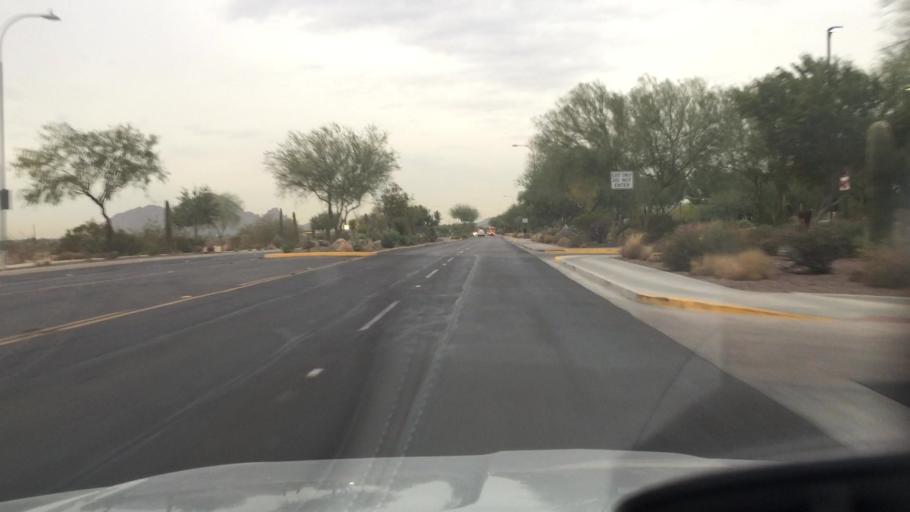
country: US
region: Arizona
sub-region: Maricopa County
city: Scottsdale
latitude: 33.5386
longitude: -111.8693
